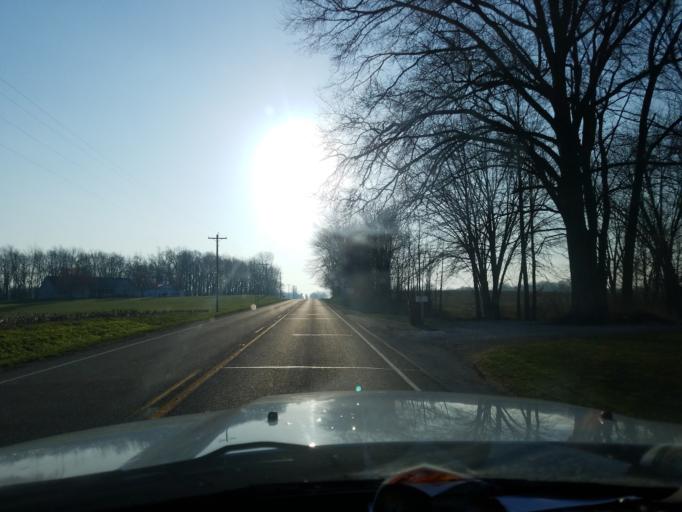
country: US
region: Indiana
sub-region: Vigo County
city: Seelyville
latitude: 39.3898
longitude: -87.2278
